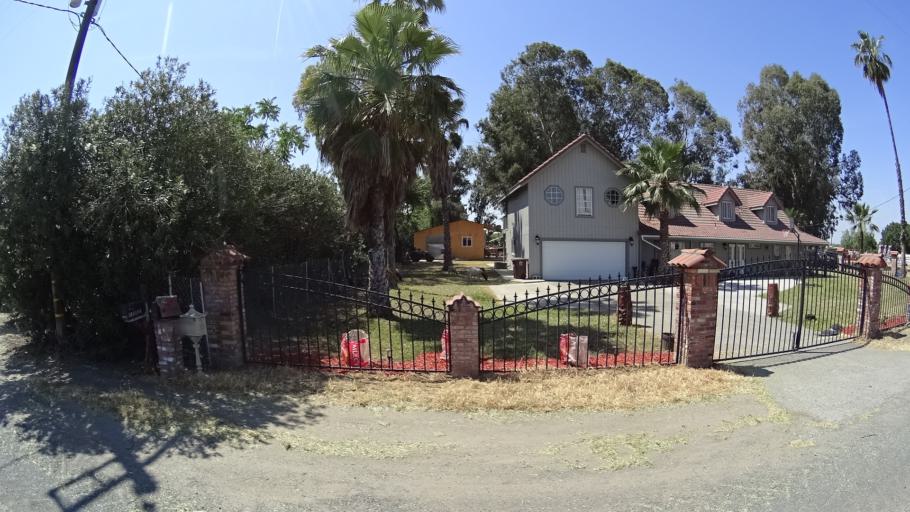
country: US
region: California
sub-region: Fresno County
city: Riverdale
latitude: 36.4020
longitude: -119.8501
